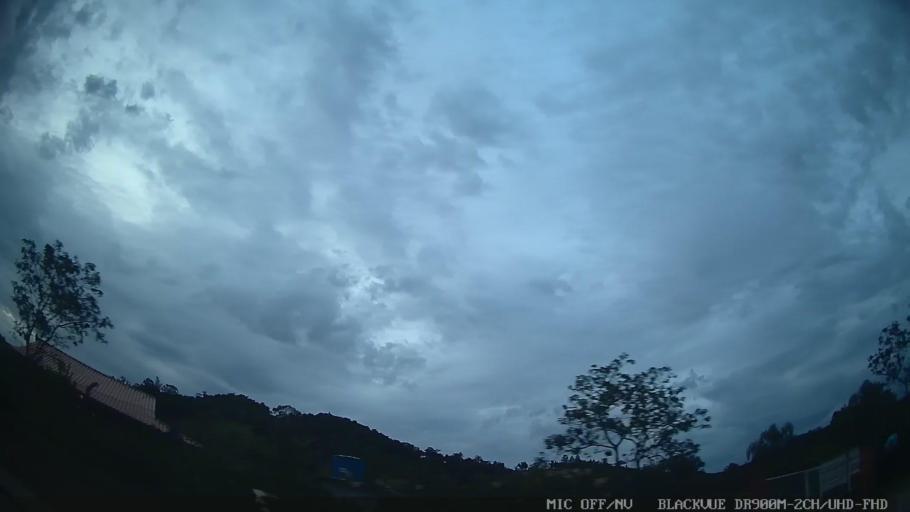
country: BR
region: Sao Paulo
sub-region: Amparo
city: Amparo
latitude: -22.8410
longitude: -46.7733
